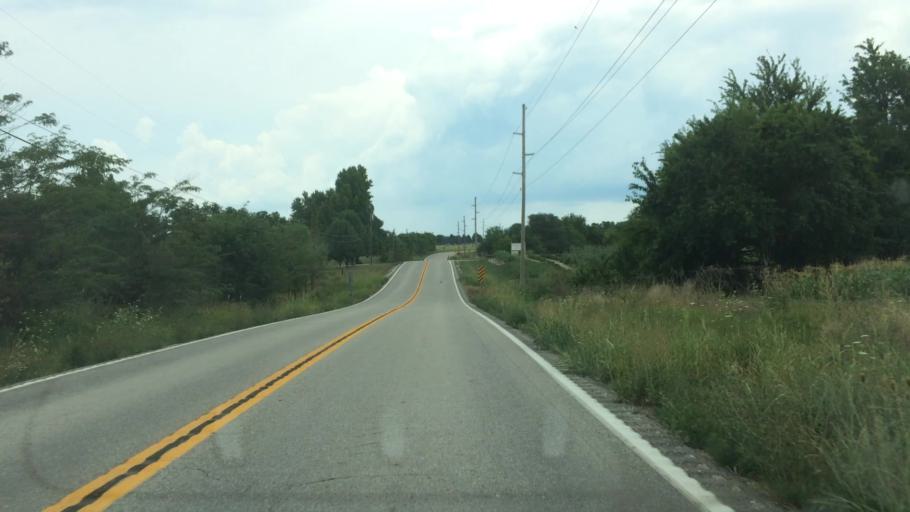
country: US
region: Missouri
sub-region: Greene County
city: Strafford
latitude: 37.2402
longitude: -93.1362
